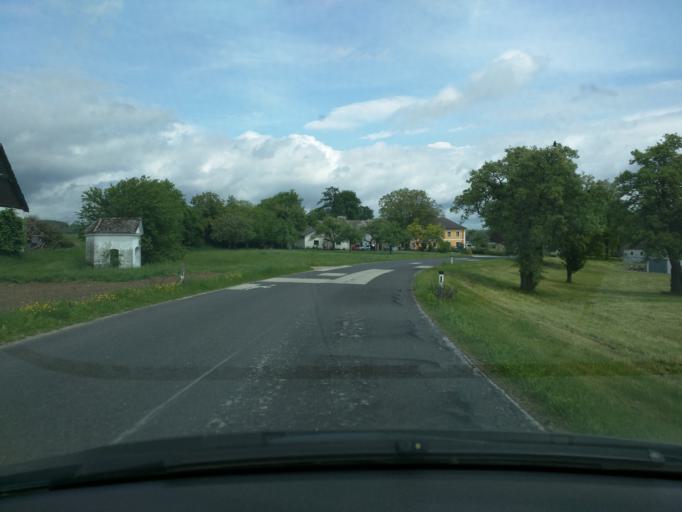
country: AT
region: Lower Austria
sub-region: Politischer Bezirk Amstetten
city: Ferschnitz
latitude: 48.1108
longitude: 15.0026
